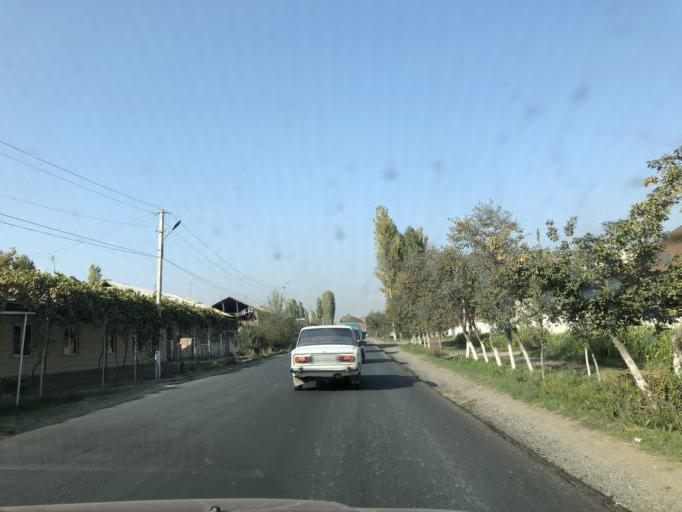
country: UZ
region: Namangan
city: Chust Shahri
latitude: 41.0685
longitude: 71.2047
